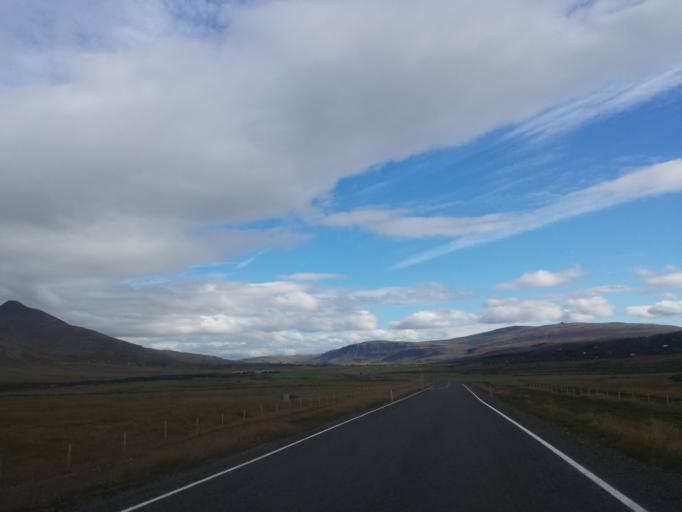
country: IS
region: West
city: Borgarnes
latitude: 64.4277
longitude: -21.6959
